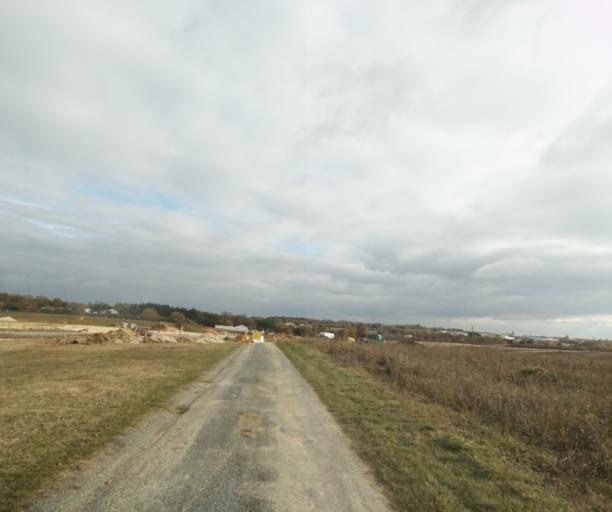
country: FR
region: Poitou-Charentes
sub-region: Departement de la Charente-Maritime
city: Saint-Georges-des-Coteaux
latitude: 45.7612
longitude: -0.6759
